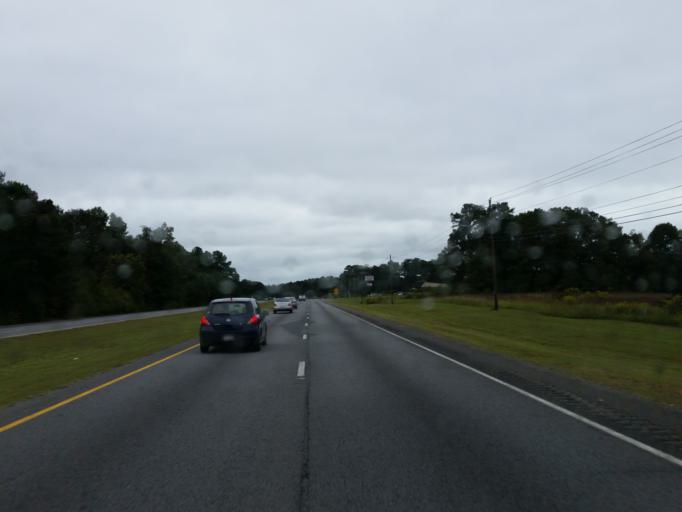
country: US
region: Georgia
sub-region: Clayton County
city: Lovejoy
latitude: 33.4360
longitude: -84.3208
